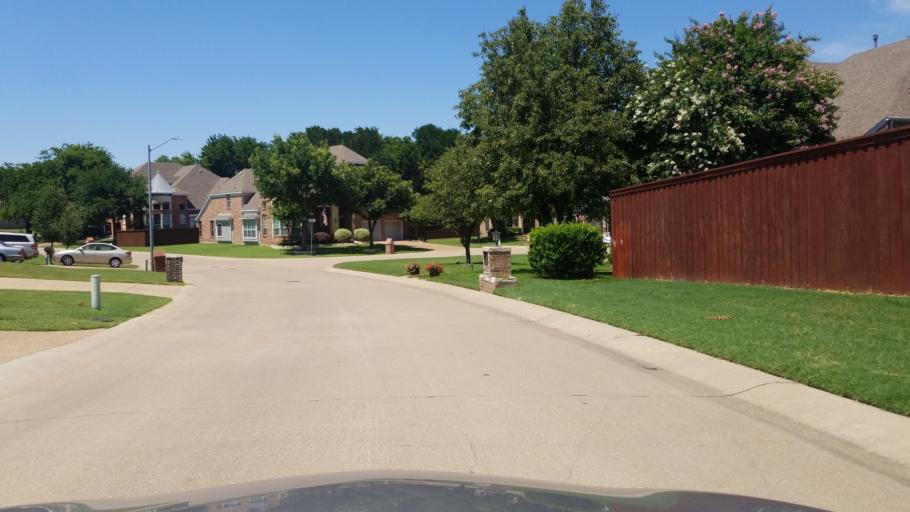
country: US
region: Texas
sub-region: Dallas County
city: Grand Prairie
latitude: 32.6814
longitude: -96.9992
